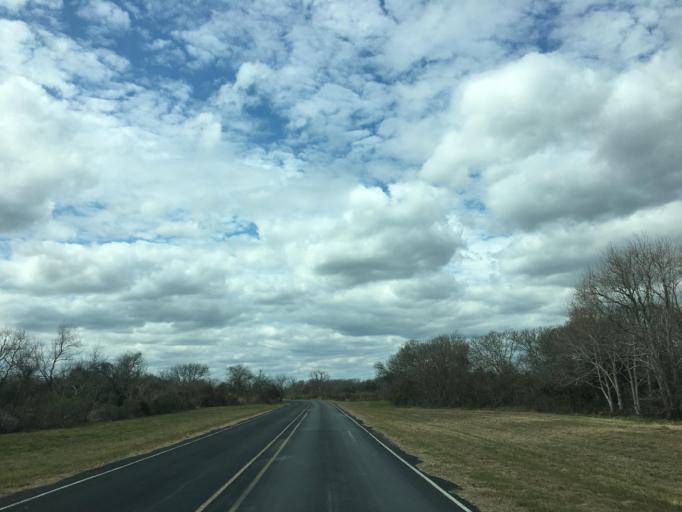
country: US
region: Texas
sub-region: Brazoria County
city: Oyster Creek
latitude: 29.0596
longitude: -95.2710
